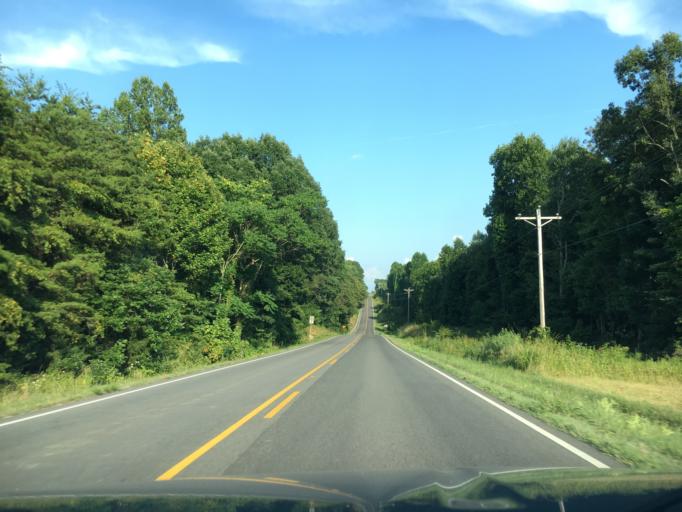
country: US
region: Virginia
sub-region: Franklin County
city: Union Hall
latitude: 36.9632
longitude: -79.5791
